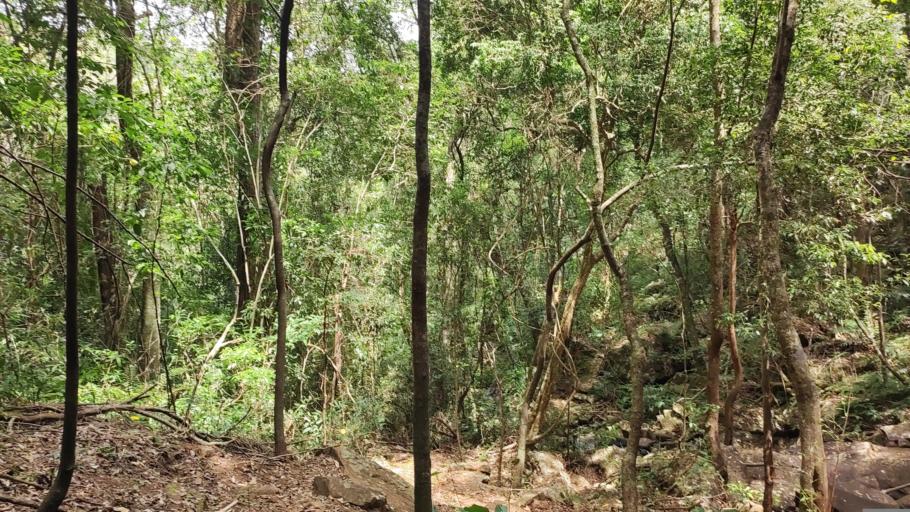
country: AR
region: Misiones
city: Dos de Mayo
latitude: -26.9966
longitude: -54.6239
